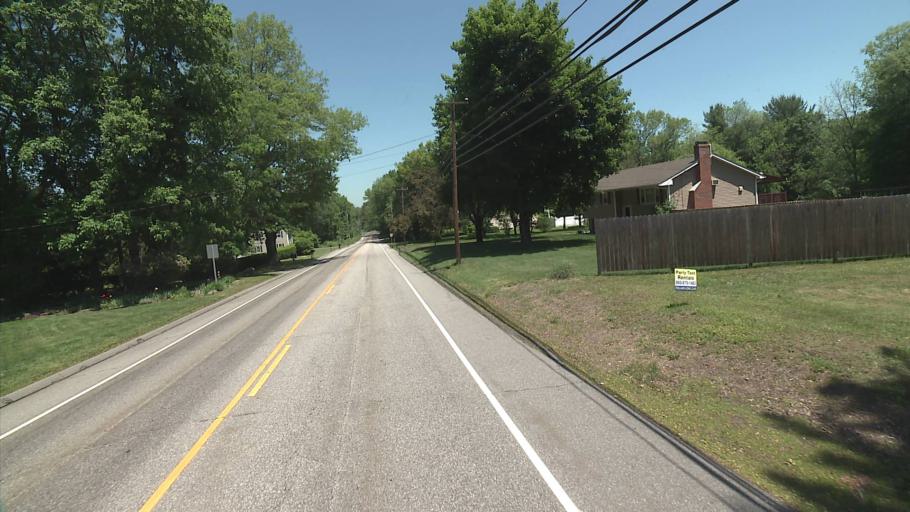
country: US
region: Connecticut
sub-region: Tolland County
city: Crystal Lake
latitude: 41.9172
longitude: -72.3899
